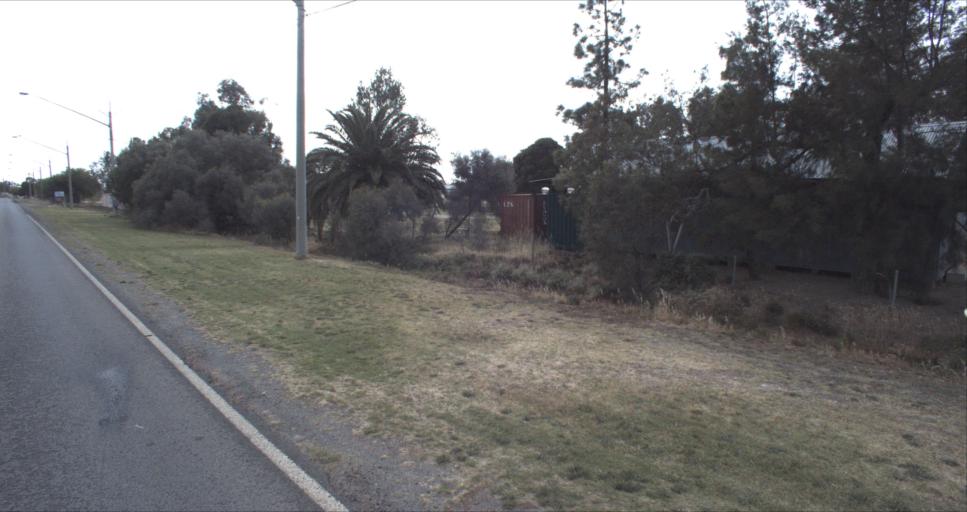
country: AU
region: New South Wales
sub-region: Leeton
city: Leeton
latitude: -34.5636
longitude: 146.3992
